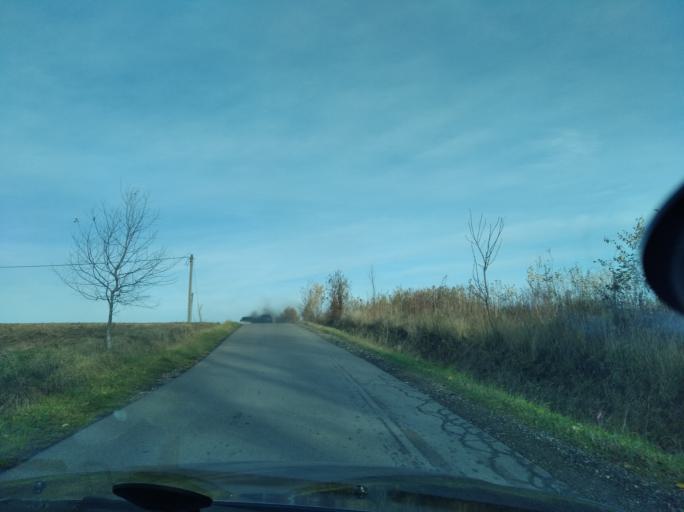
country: PL
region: Subcarpathian Voivodeship
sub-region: Powiat rzeszowski
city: Krasne
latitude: 50.0167
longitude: 22.1074
